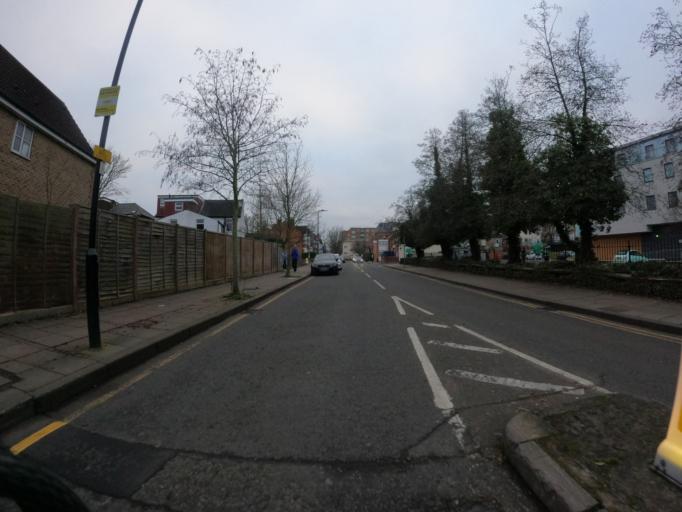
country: GB
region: England
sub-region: Greater London
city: Ealing
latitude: 51.5097
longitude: -0.3220
